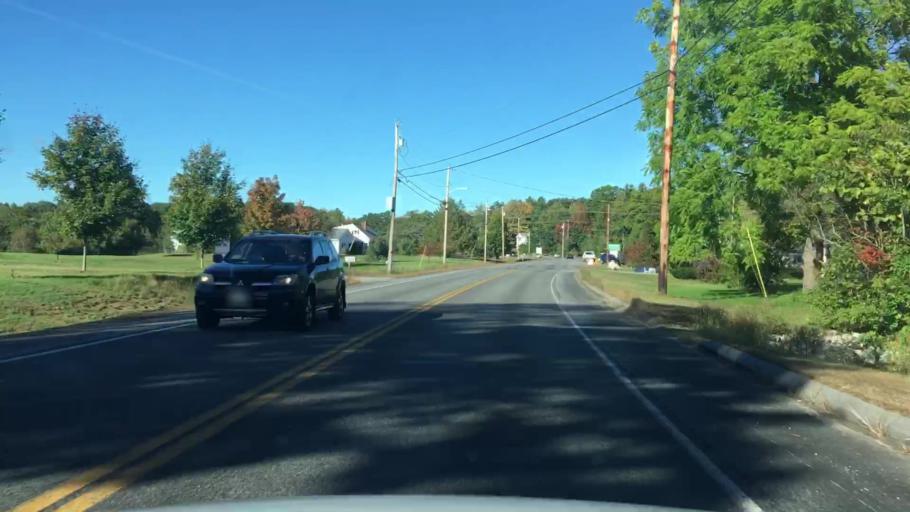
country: US
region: Maine
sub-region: Androscoggin County
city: Lisbon Falls
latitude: 44.0144
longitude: -70.0689
